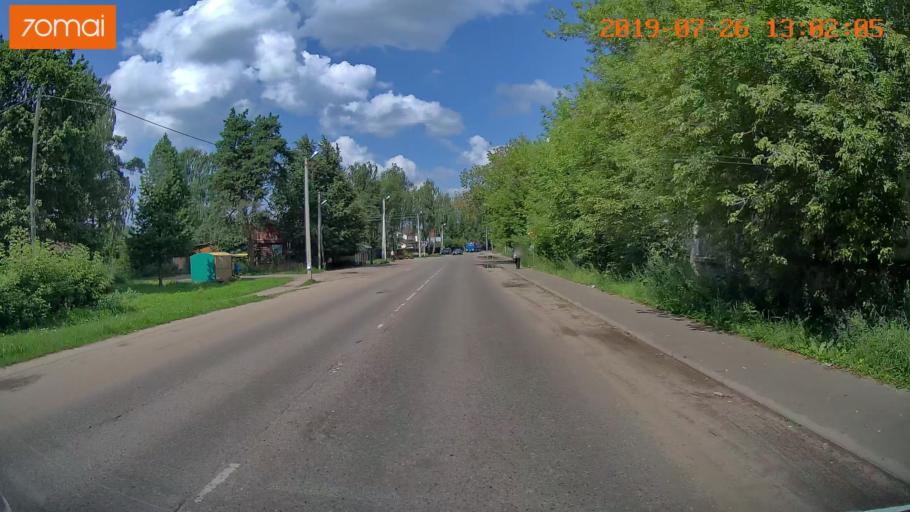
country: RU
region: Ivanovo
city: Bogorodskoye
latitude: 57.0427
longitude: 41.0117
